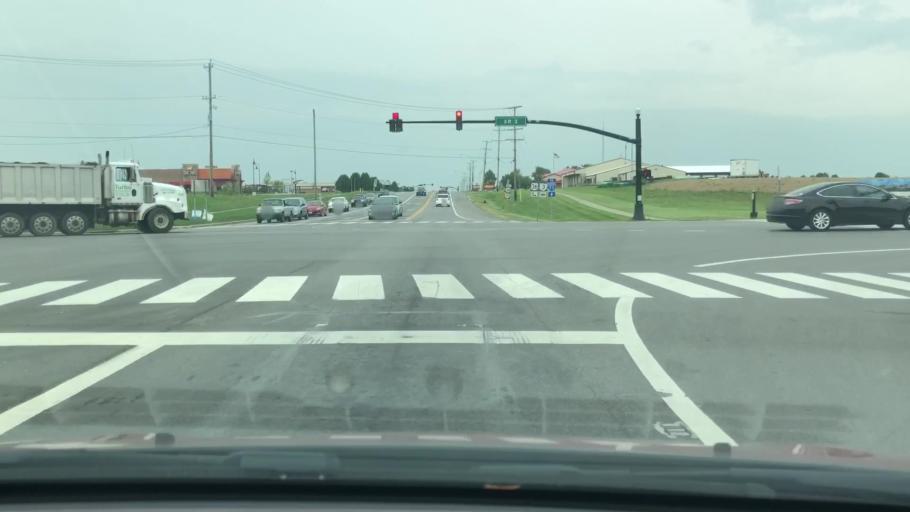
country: US
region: Ohio
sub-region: Delaware County
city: Sunbury
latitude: 40.2454
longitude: -82.8644
